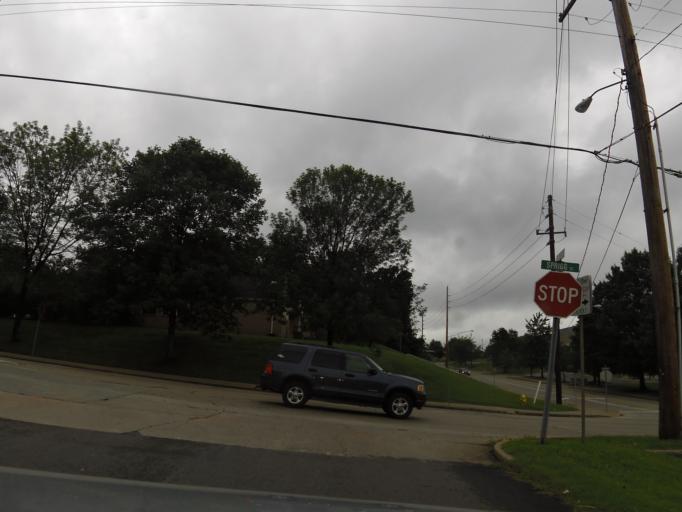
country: US
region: Missouri
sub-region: Cape Girardeau County
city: Cape Girardeau
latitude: 37.3183
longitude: -89.5248
